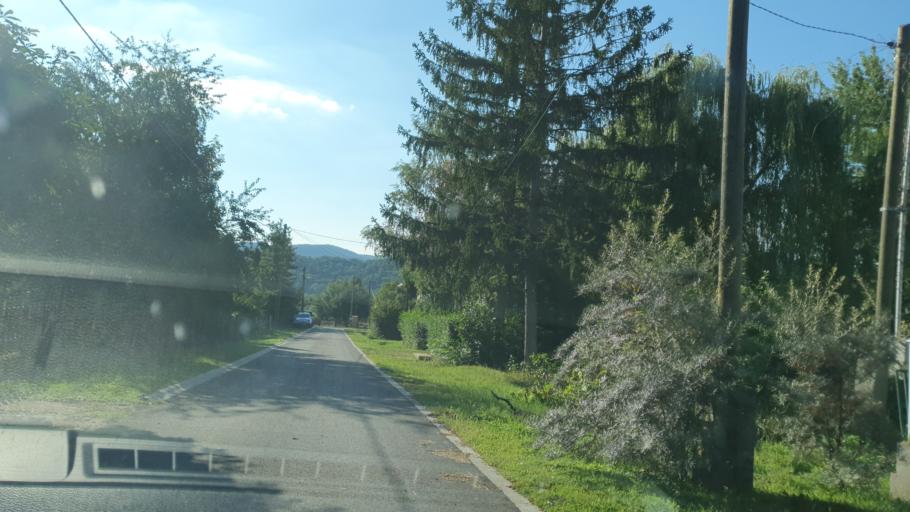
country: HU
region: Nograd
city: Paszto
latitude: 47.9794
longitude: 19.6393
